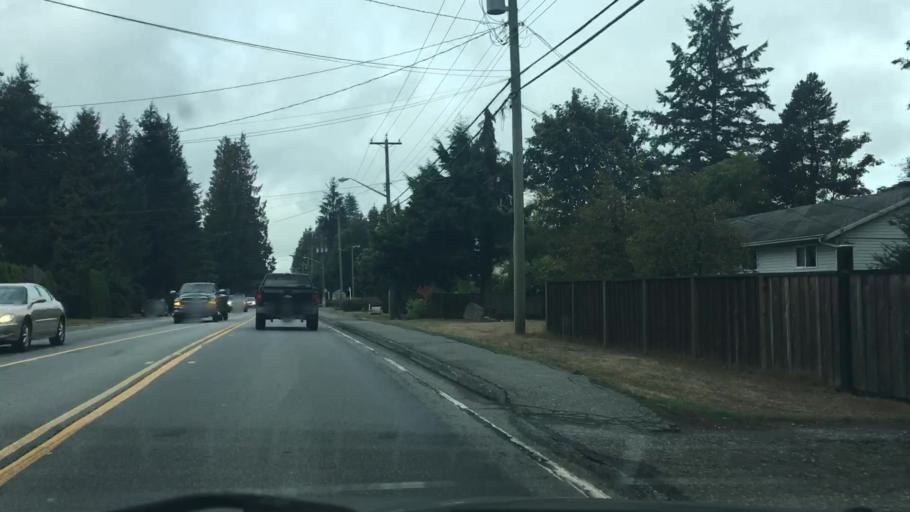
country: CA
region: British Columbia
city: Langley
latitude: 49.1041
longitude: -122.5383
